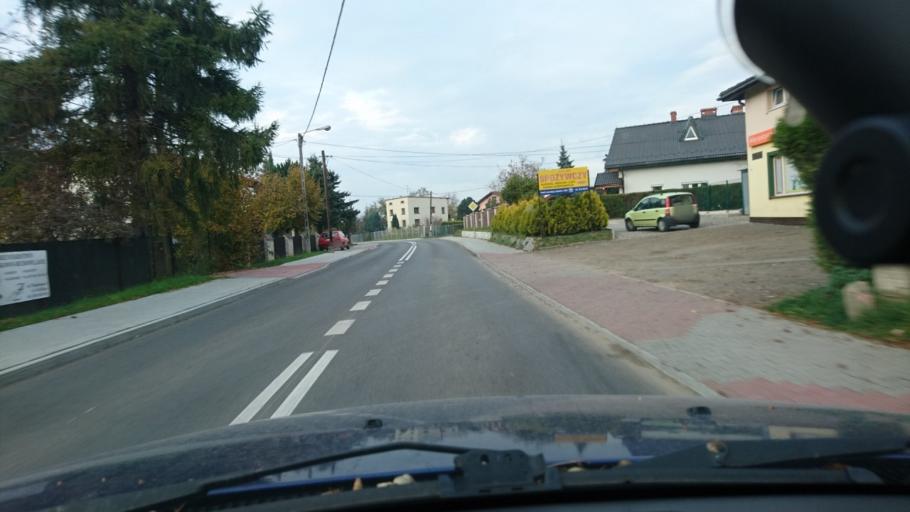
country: PL
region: Silesian Voivodeship
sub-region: Powiat bielski
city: Kozy
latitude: 49.8432
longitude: 19.1171
